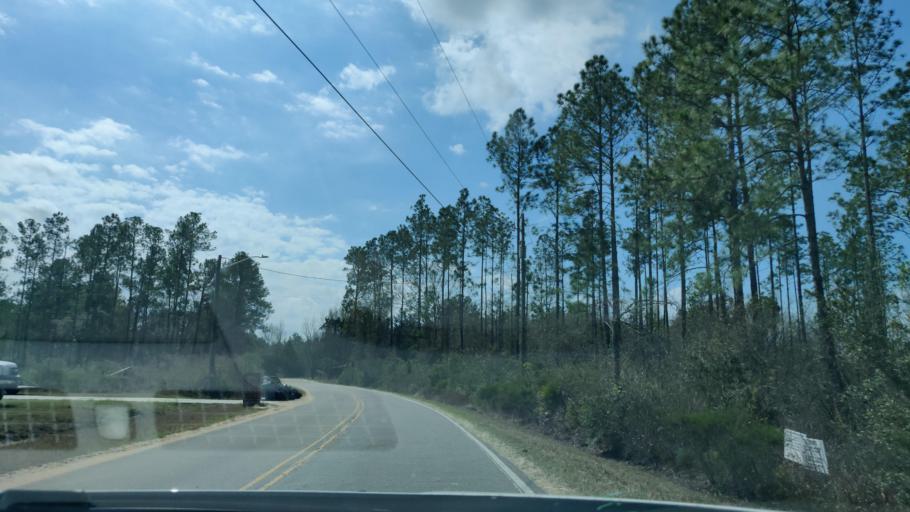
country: US
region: Florida
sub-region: Duval County
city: Baldwin
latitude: 30.1877
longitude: -81.9698
